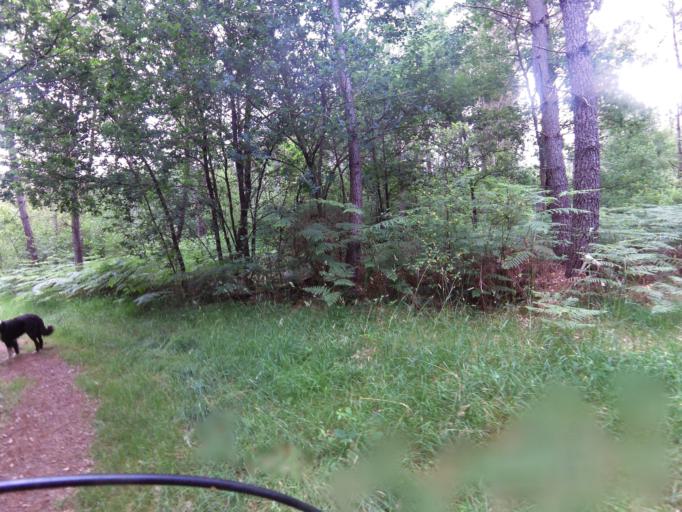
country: FR
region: Brittany
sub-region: Departement du Morbihan
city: Molac
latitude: 47.7594
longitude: -2.4265
